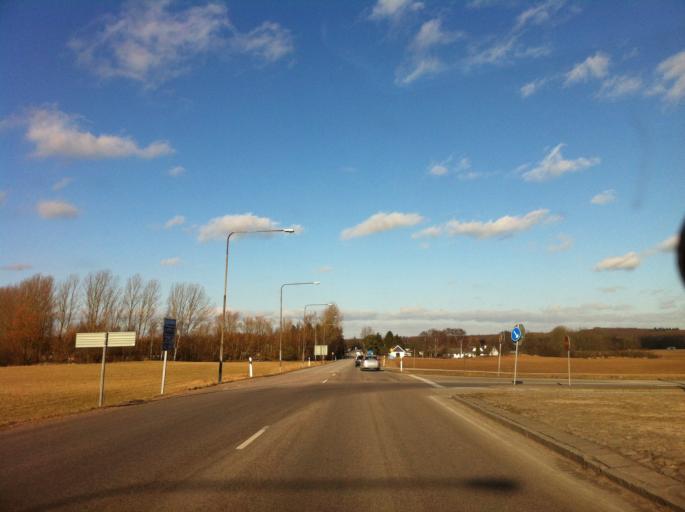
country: SE
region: Skane
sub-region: Svedala Kommun
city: Svedala
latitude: 55.5159
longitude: 13.2492
